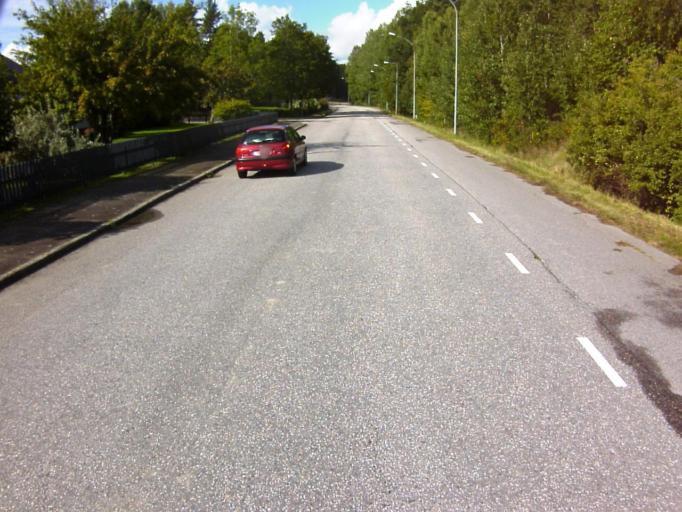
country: SE
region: Soedermanland
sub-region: Eskilstuna Kommun
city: Eskilstuna
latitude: 59.3978
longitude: 16.5407
